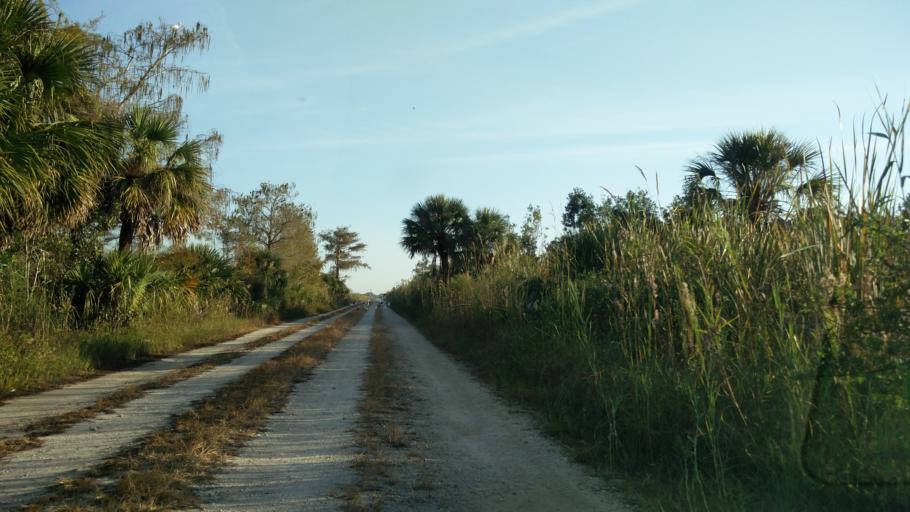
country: US
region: Florida
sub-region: Collier County
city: Lely Resort
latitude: 25.9732
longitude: -81.3686
